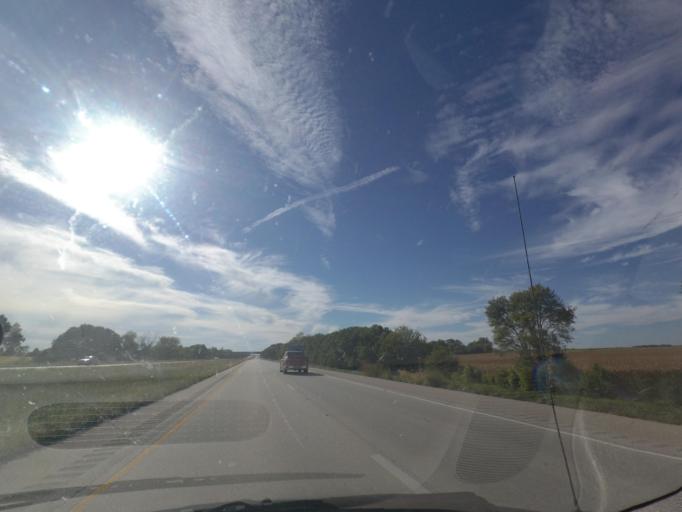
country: US
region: Illinois
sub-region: Macon County
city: Forsyth
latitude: 39.9098
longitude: -88.9138
